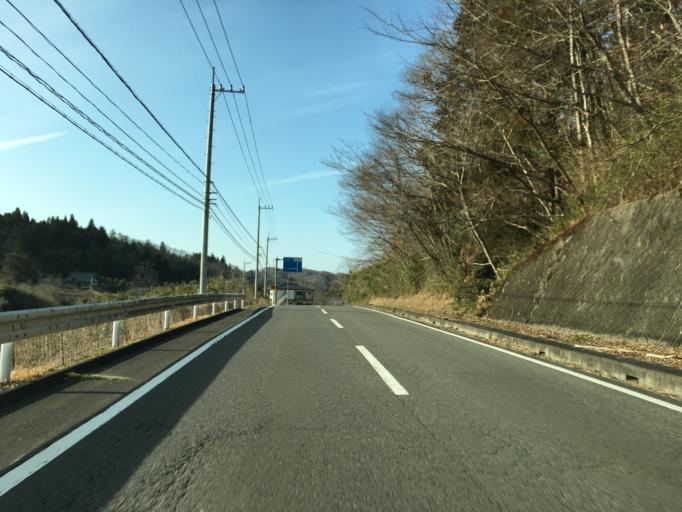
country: JP
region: Ibaraki
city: Daigo
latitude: 36.7621
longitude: 140.4346
